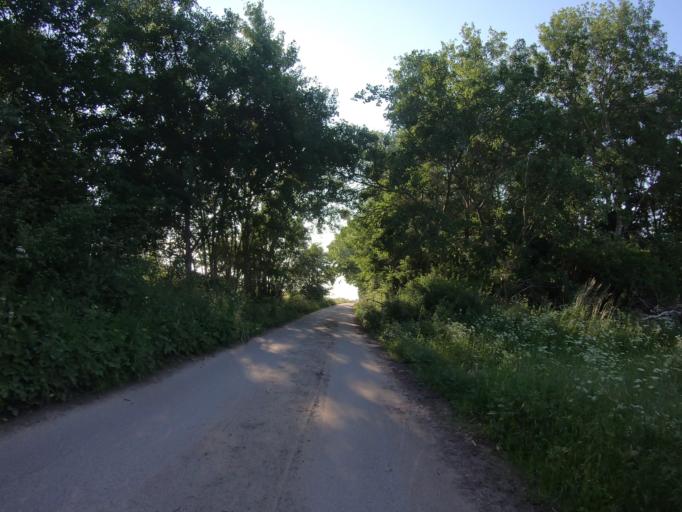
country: DE
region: Lower Saxony
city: Vordorf
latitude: 52.3546
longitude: 10.5461
